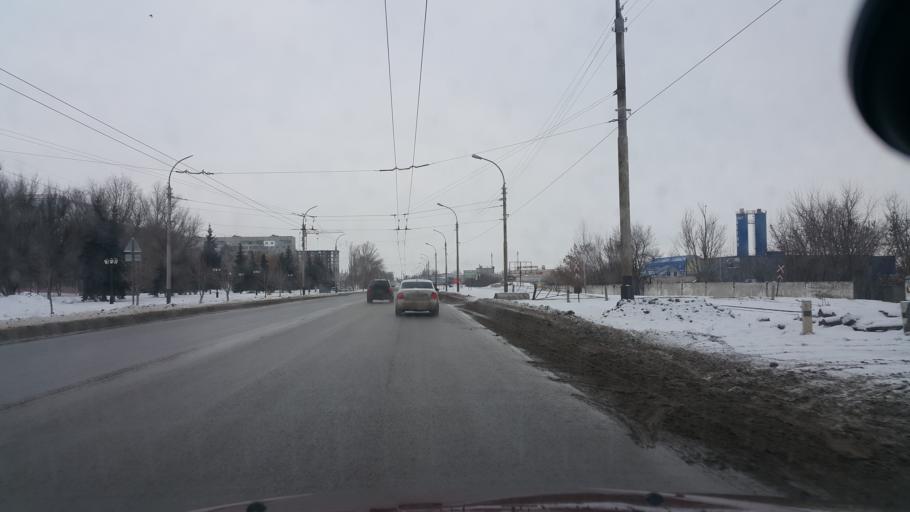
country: RU
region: Tambov
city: Tambov
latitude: 52.7366
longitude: 41.3857
